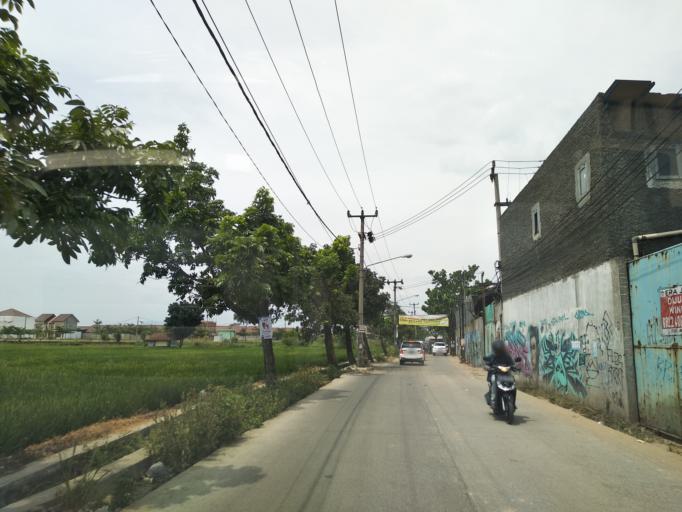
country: ID
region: West Java
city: Pameungpeuk
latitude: -6.9697
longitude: 107.6377
